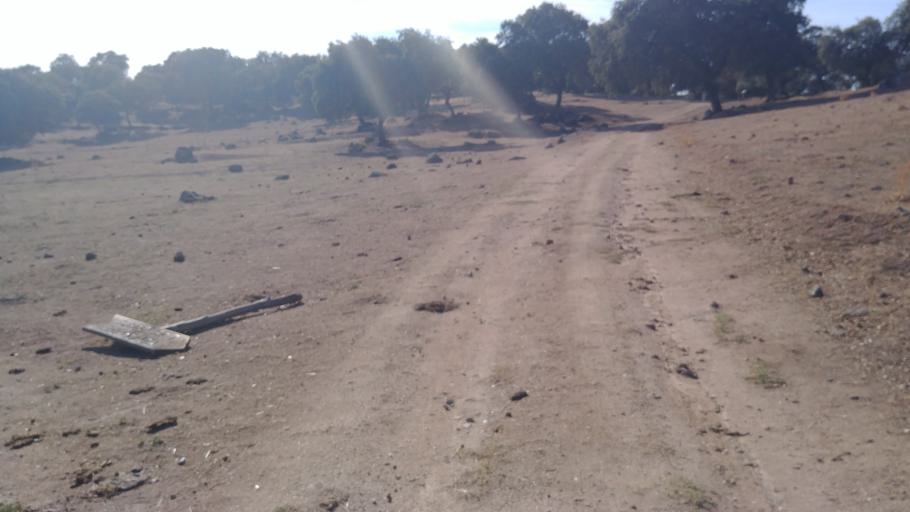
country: ES
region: Castille-La Mancha
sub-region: Province of Toledo
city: Navalcan
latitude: 40.0658
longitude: -5.1181
